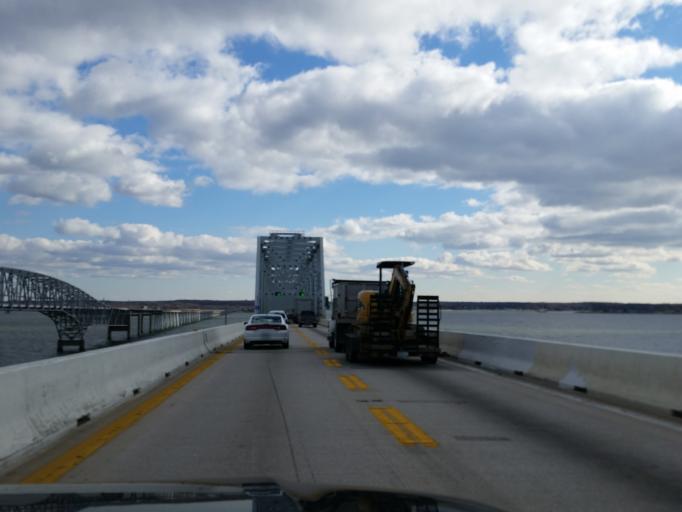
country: US
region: Maryland
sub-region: Queen Anne's County
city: Stevensville
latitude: 38.9887
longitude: -76.3628
